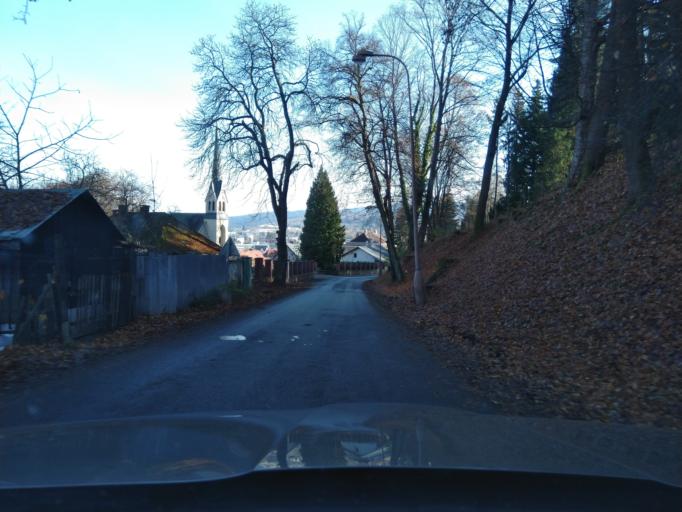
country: CZ
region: Jihocesky
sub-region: Okres Prachatice
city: Vimperk
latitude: 49.0567
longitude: 13.7748
